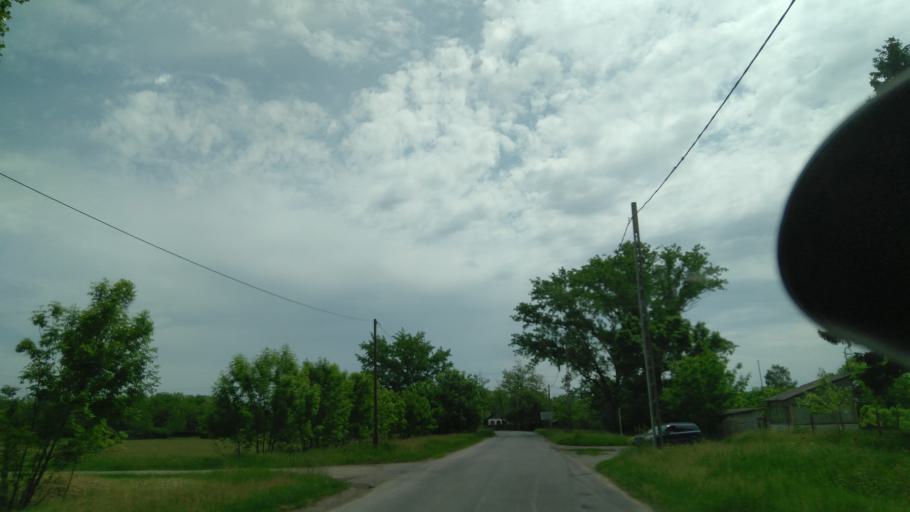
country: HU
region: Bekes
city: Fuzesgyarmat
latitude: 47.0984
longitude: 21.2294
